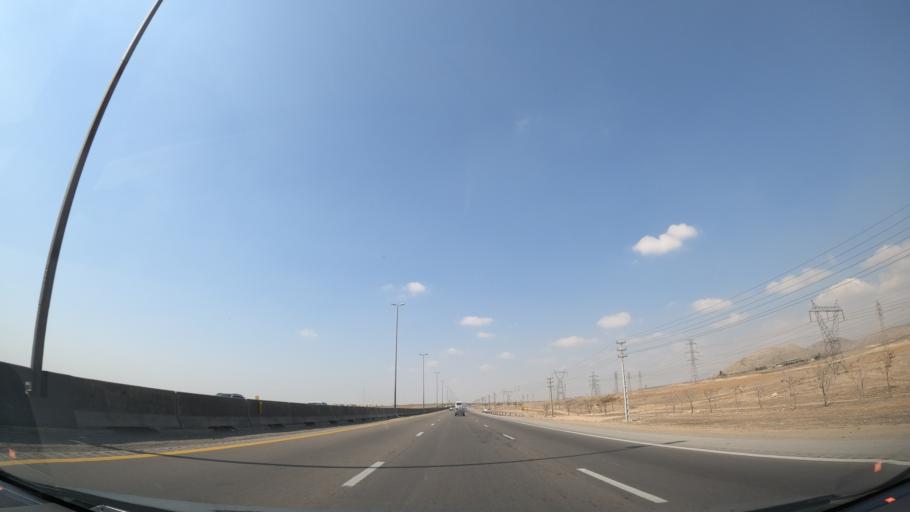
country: IR
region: Qazvin
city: Abyek
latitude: 36.0603
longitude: 50.4981
